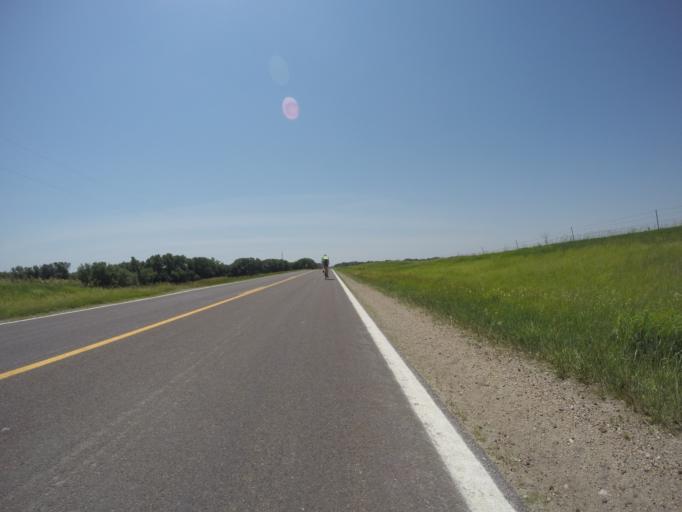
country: US
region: Nebraska
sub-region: Pawnee County
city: Pawnee City
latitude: 40.0117
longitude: -96.0484
